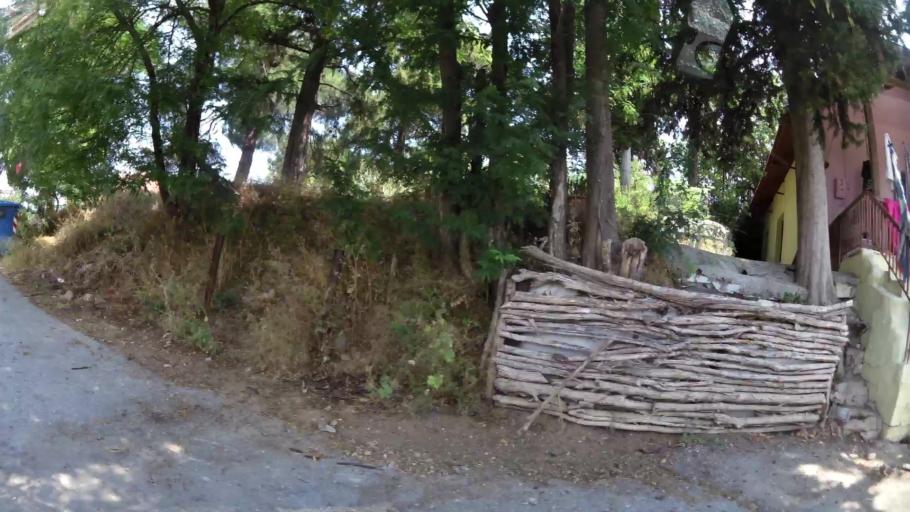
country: GR
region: Central Macedonia
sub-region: Nomos Imathias
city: Veroia
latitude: 40.5146
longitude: 22.1986
